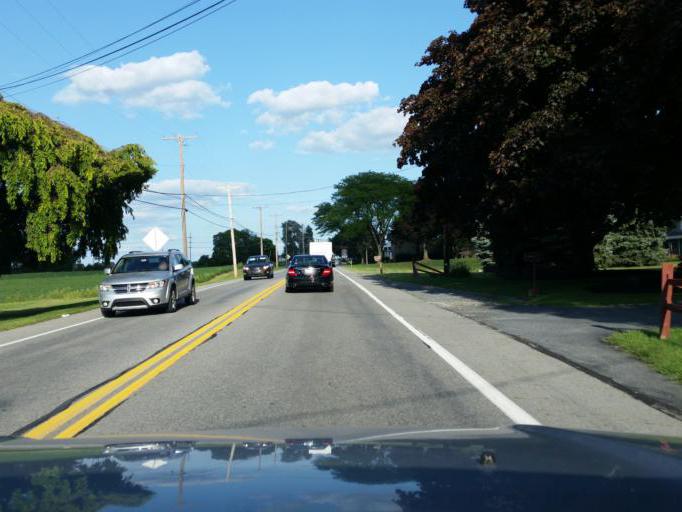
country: US
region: Pennsylvania
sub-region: Lebanon County
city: Campbelltown
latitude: 40.2771
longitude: -76.6069
